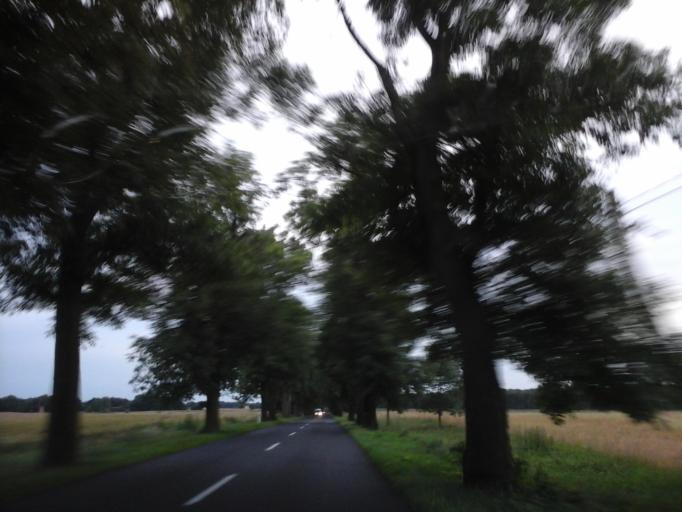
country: PL
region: West Pomeranian Voivodeship
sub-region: Powiat goleniowski
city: Maszewo
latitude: 53.5297
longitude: 15.1141
